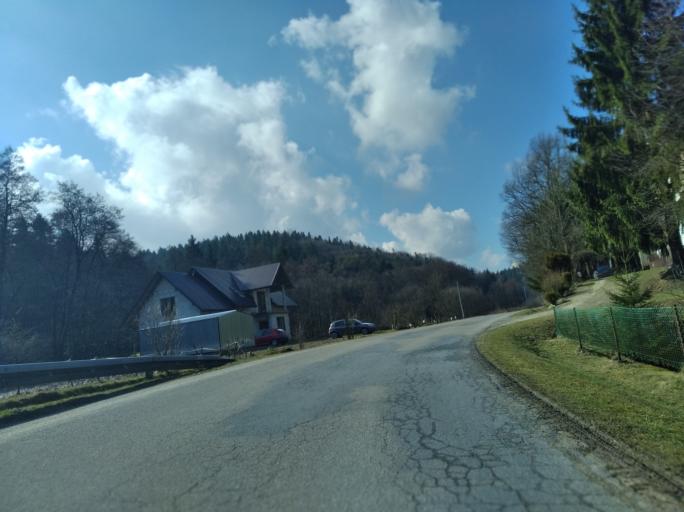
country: PL
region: Subcarpathian Voivodeship
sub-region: Powiat strzyzowski
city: Frysztak
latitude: 49.8663
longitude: 21.5598
